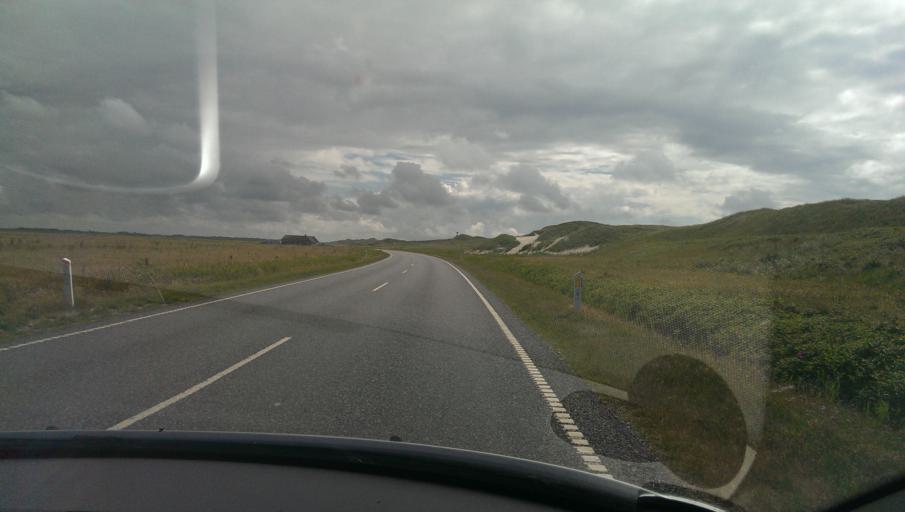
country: DK
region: Central Jutland
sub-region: Ringkobing-Skjern Kommune
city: Ringkobing
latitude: 56.1873
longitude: 8.1263
